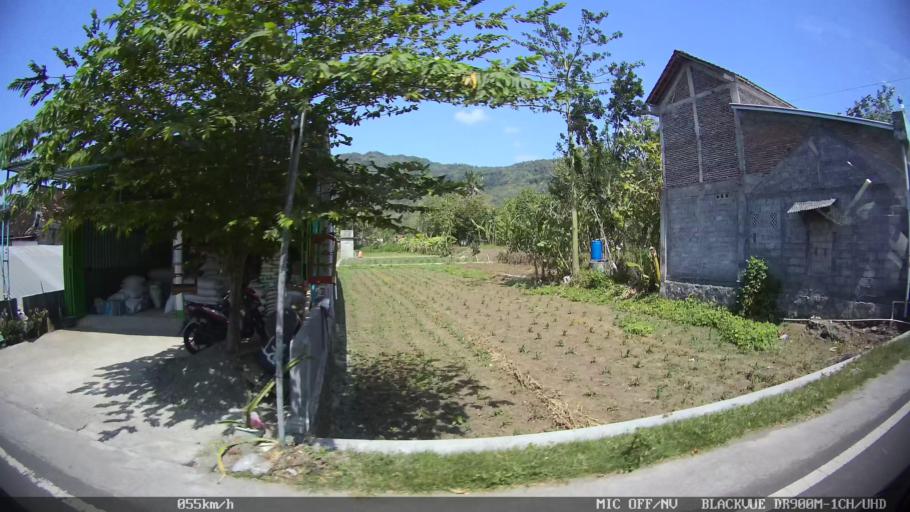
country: ID
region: Daerah Istimewa Yogyakarta
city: Pundong
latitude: -7.9674
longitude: 110.3534
